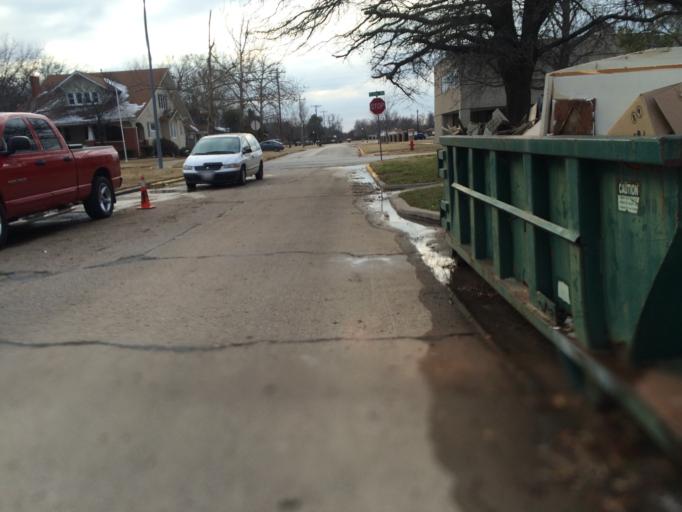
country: US
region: Oklahoma
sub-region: Cleveland County
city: Norman
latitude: 35.2190
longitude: -97.4397
